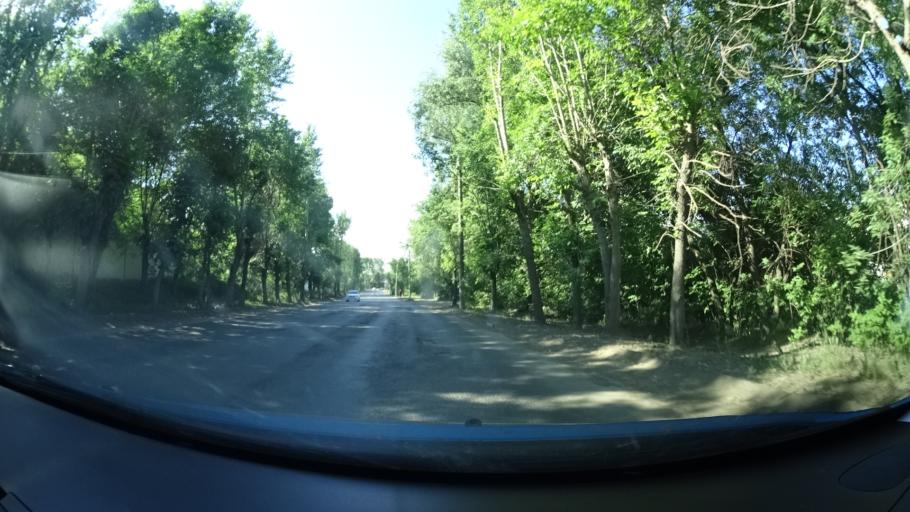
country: RU
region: Bashkortostan
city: Ufa
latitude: 54.8383
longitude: 56.0757
